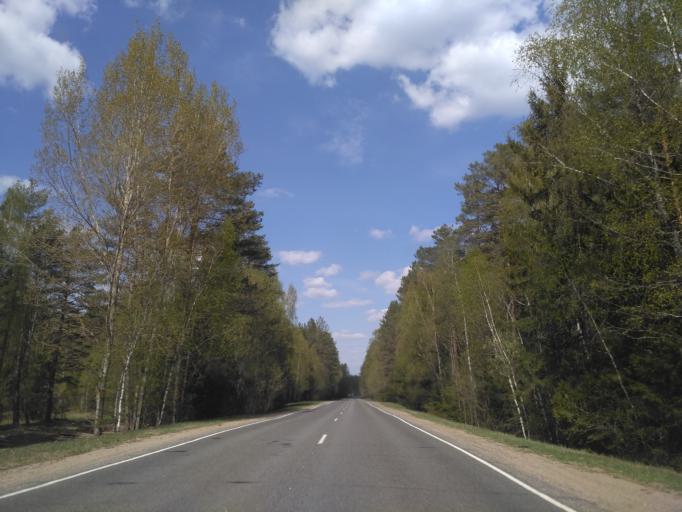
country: BY
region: Minsk
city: Myadzyel
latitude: 54.8132
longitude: 26.9413
